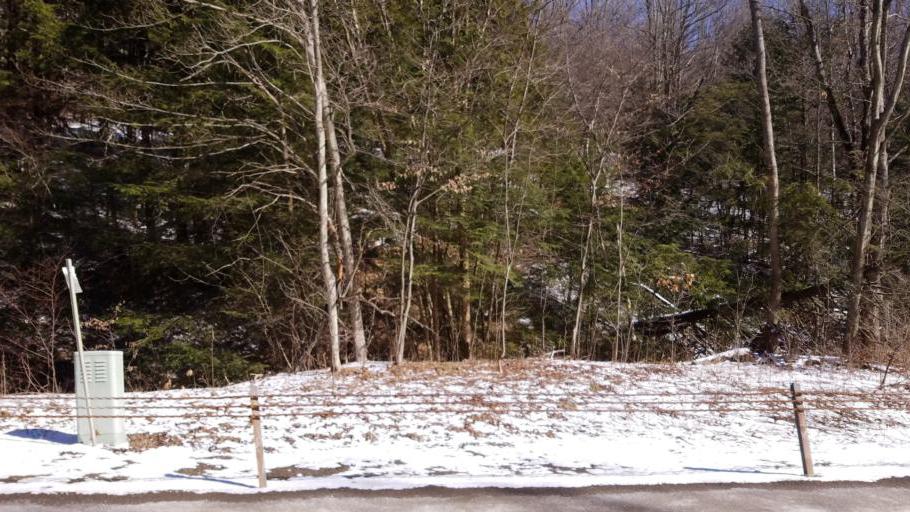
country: US
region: New York
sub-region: Allegany County
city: Andover
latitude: 42.0482
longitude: -77.7901
